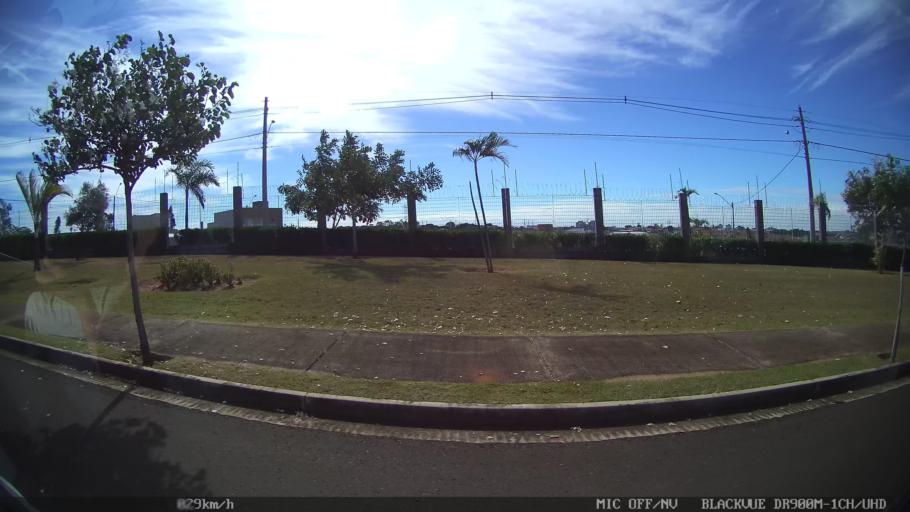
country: BR
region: Sao Paulo
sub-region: Sao Jose Do Rio Preto
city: Sao Jose do Rio Preto
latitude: -20.8517
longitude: -49.3736
